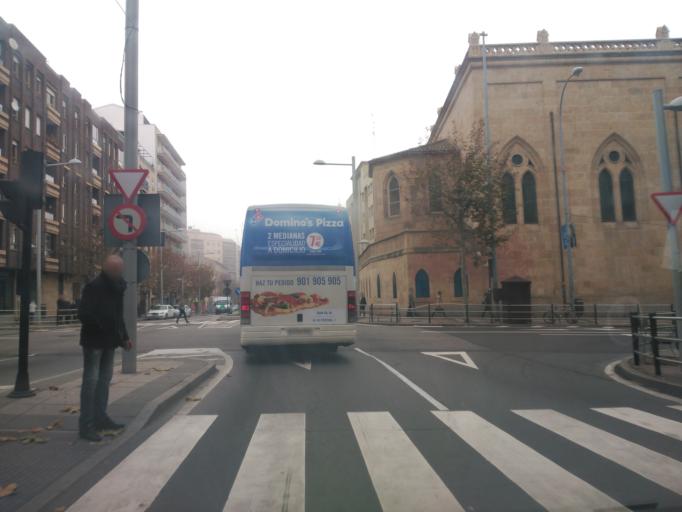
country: ES
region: Castille and Leon
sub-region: Provincia de Salamanca
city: Salamanca
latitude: 40.9713
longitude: -5.6584
